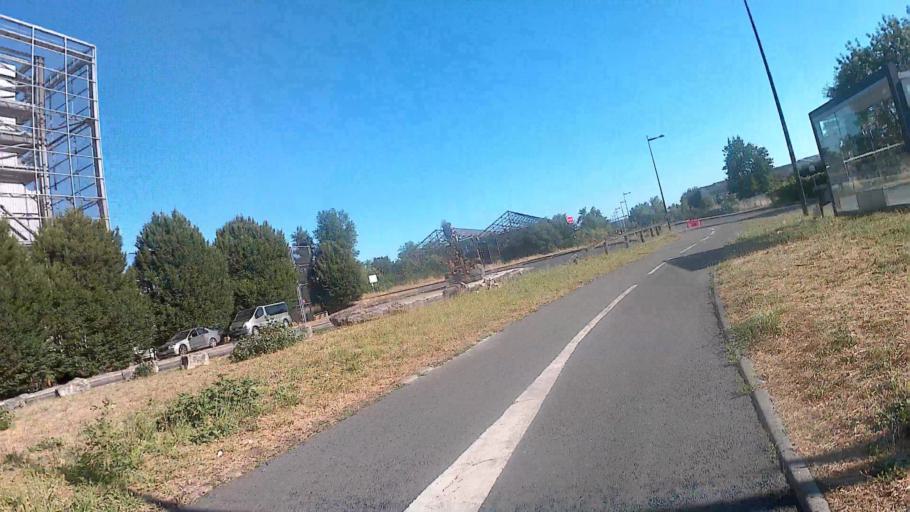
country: FR
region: Aquitaine
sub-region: Departement de la Gironde
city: Begles
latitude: 44.7999
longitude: -0.5305
